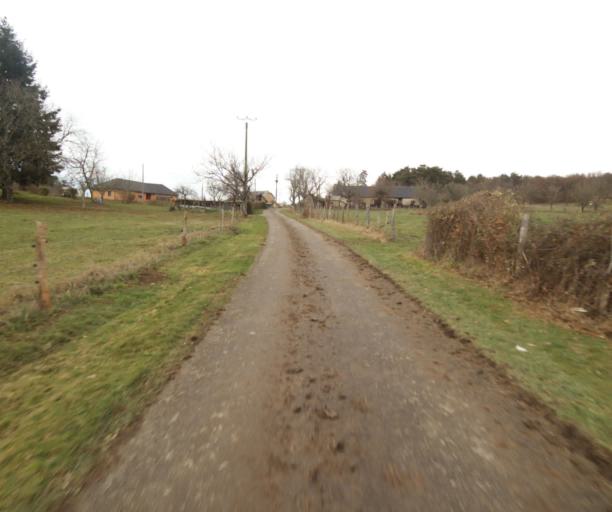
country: FR
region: Limousin
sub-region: Departement de la Correze
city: Chameyrat
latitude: 45.2470
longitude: 1.6749
